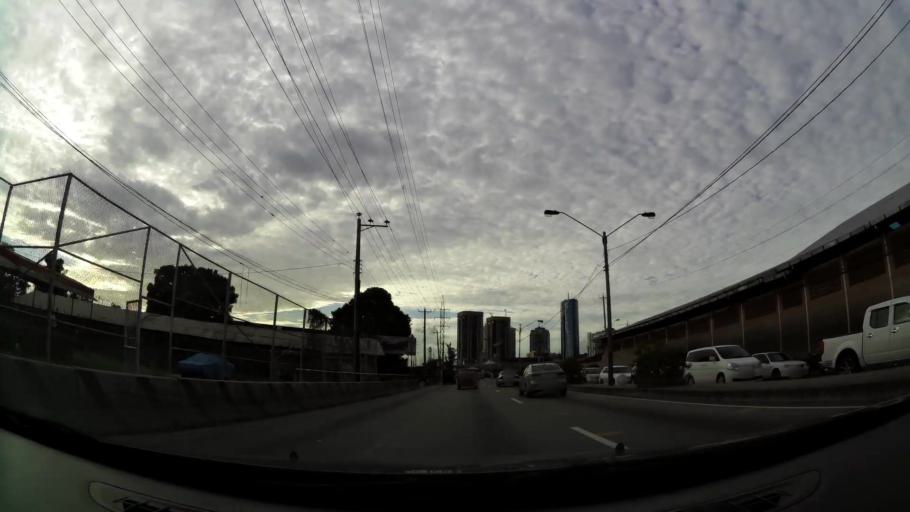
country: TT
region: San Juan/Laventille
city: Laventille
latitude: 10.6468
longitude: -61.5069
